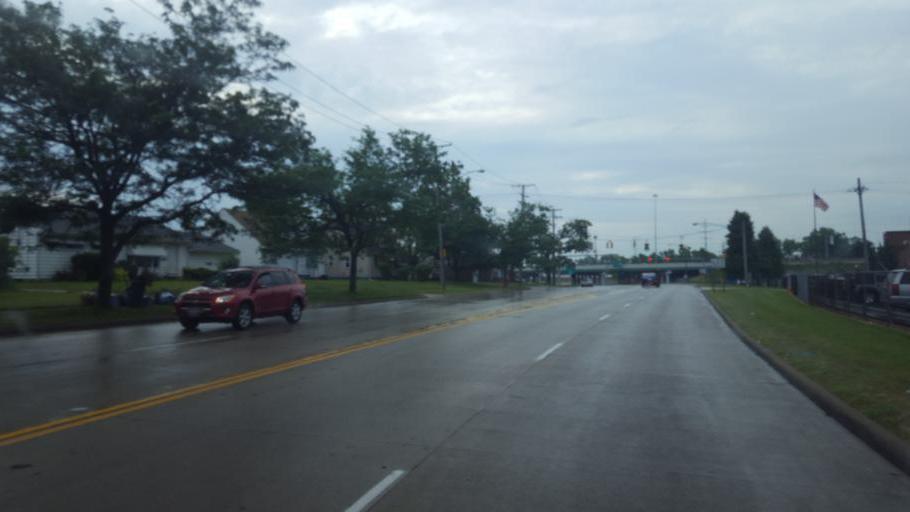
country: US
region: Ohio
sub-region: Cuyahoga County
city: North Randall
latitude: 41.4264
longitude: -81.5236
